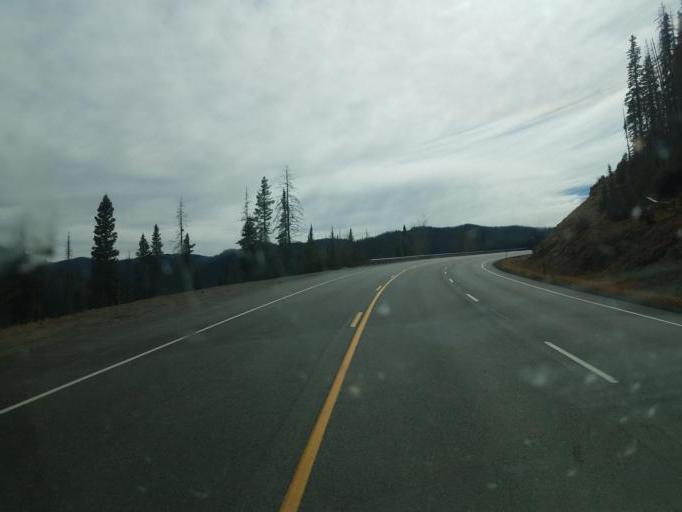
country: US
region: Colorado
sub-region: Archuleta County
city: Pagosa Springs
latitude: 37.4932
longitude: -106.7662
